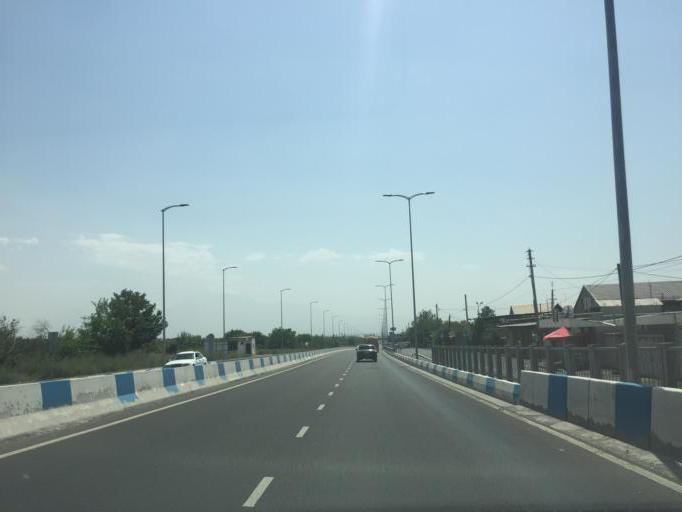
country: AM
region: Ararat
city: Norabats'
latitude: 40.1215
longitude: 44.4834
